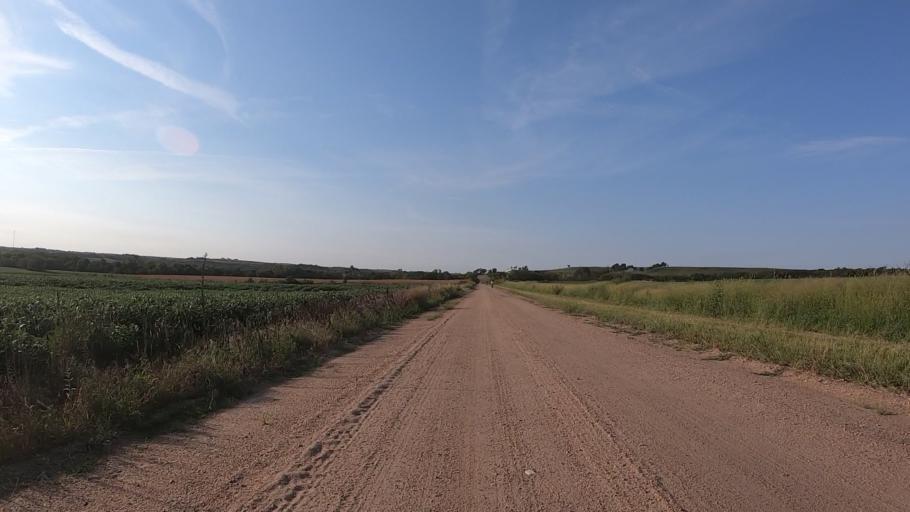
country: US
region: Kansas
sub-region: Marshall County
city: Blue Rapids
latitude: 39.6954
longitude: -96.7792
